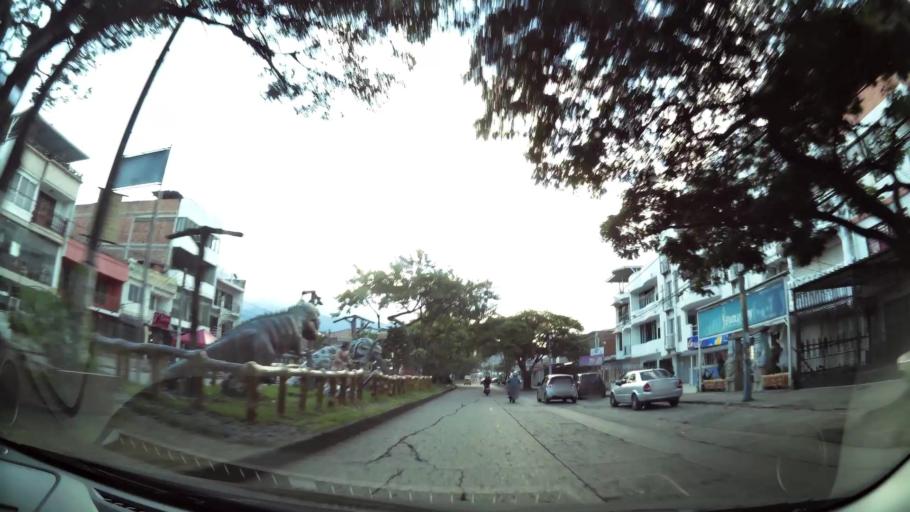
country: CO
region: Valle del Cauca
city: Cali
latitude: 3.4289
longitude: -76.5173
